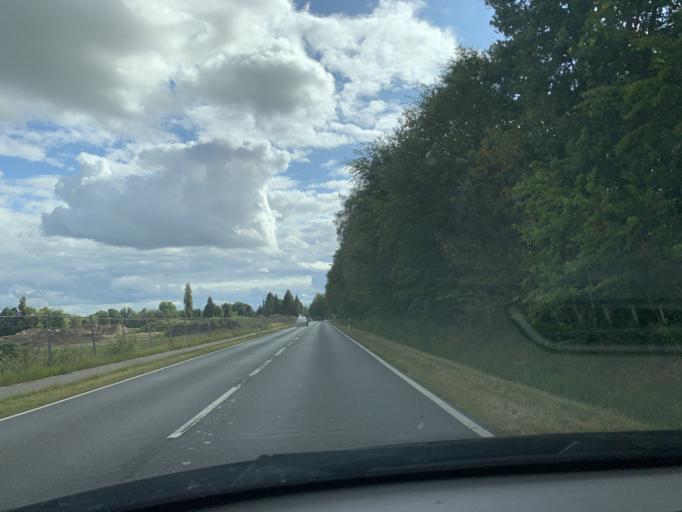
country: DE
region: Lower Saxony
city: Bad Zwischenahn
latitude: 53.2025
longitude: 7.9973
